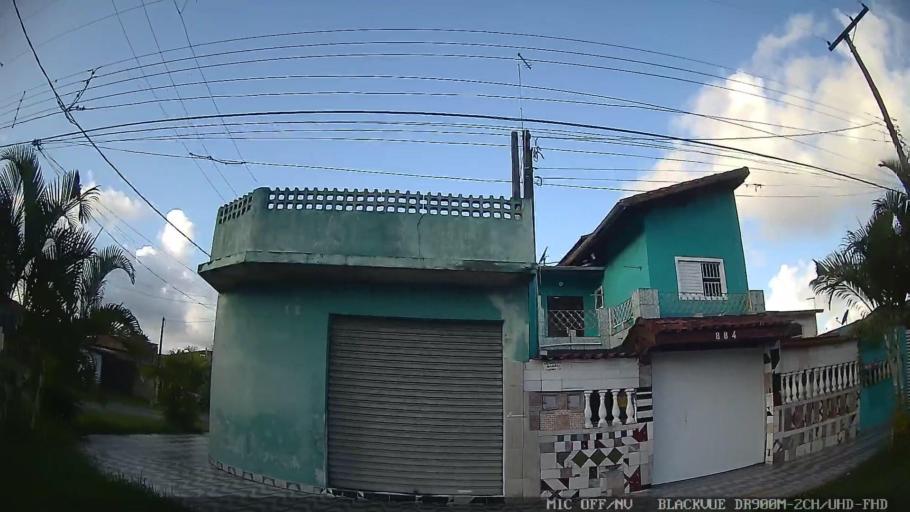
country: BR
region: Sao Paulo
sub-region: Itanhaem
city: Itanhaem
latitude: -24.1399
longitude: -46.7211
